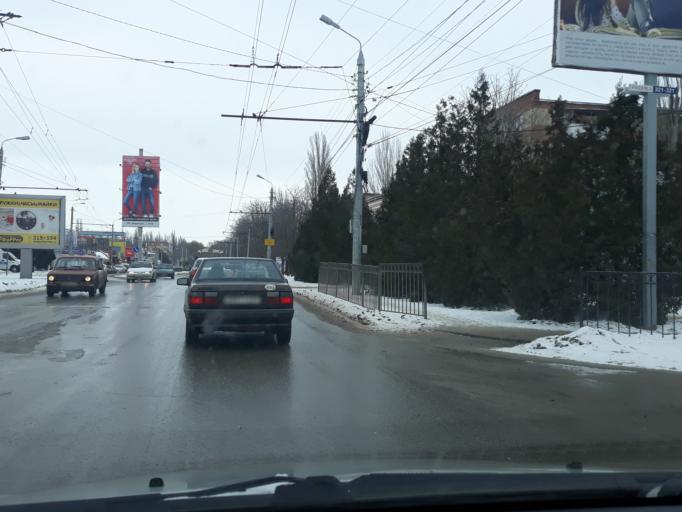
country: RU
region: Rostov
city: Taganrog
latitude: 47.2495
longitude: 38.9179
